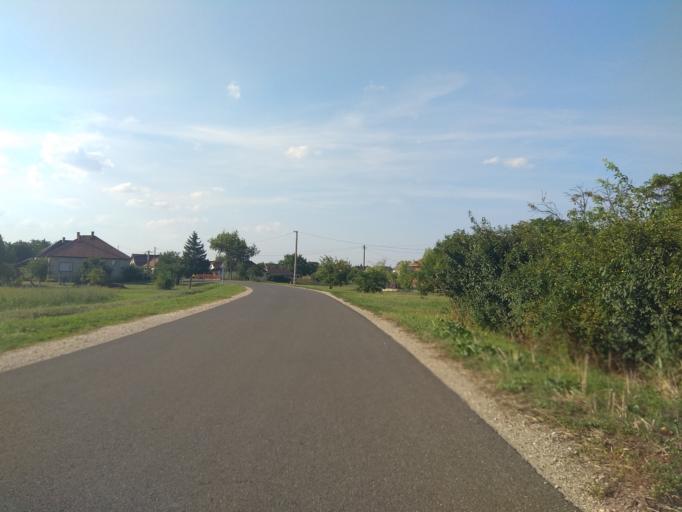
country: HU
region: Borsod-Abauj-Zemplen
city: Emod
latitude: 47.8851
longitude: 20.7698
